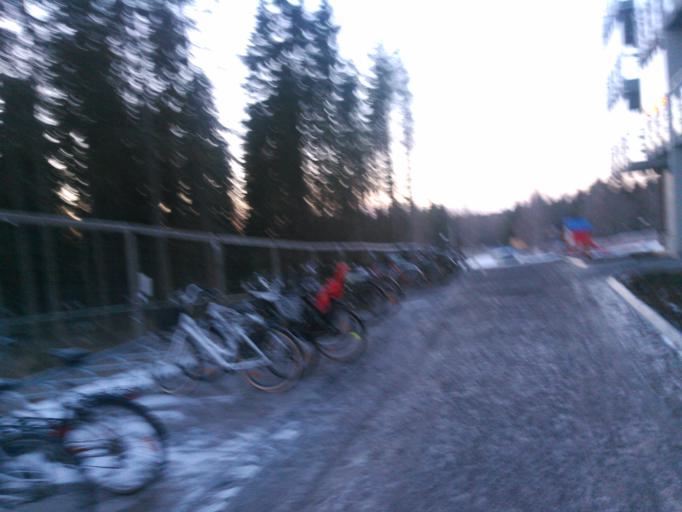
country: SE
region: Vaesterbotten
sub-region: Umea Kommun
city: Ersmark
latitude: 63.8303
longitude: 20.3249
